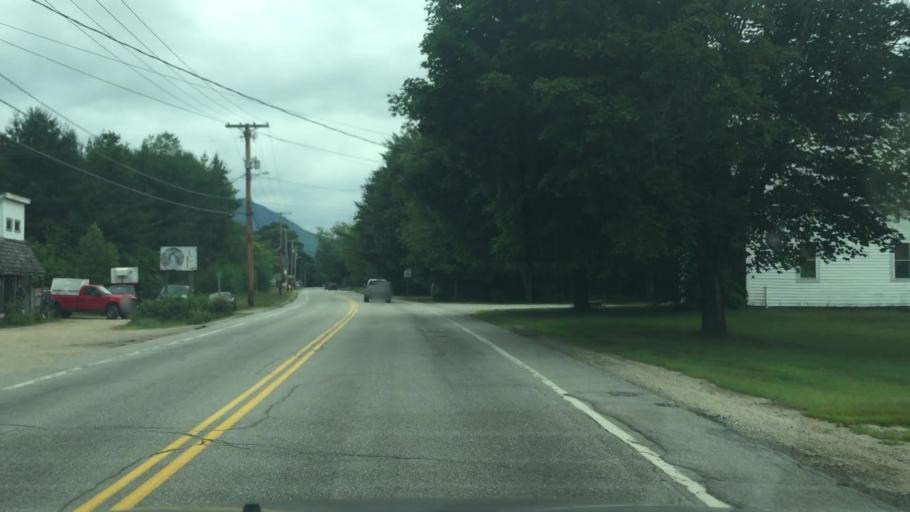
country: US
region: New Hampshire
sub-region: Carroll County
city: North Conway
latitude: 44.0783
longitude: -71.2720
